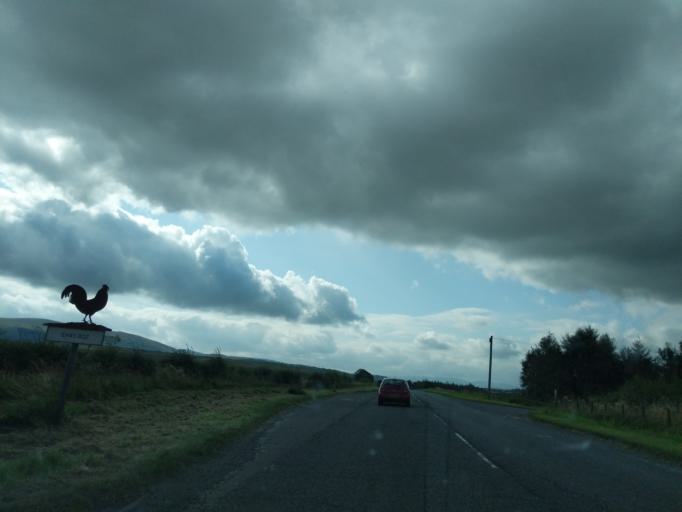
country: GB
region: Scotland
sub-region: Midlothian
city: Penicuik
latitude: 55.7643
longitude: -3.2079
